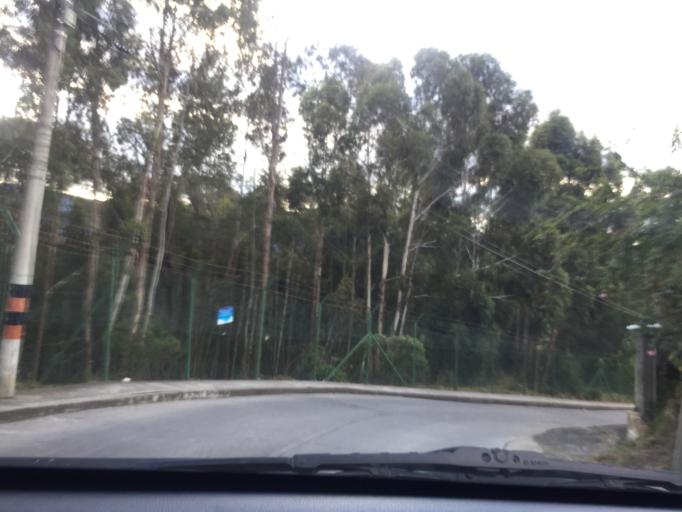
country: CO
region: Cundinamarca
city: Sopo
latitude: 4.9123
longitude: -73.9378
